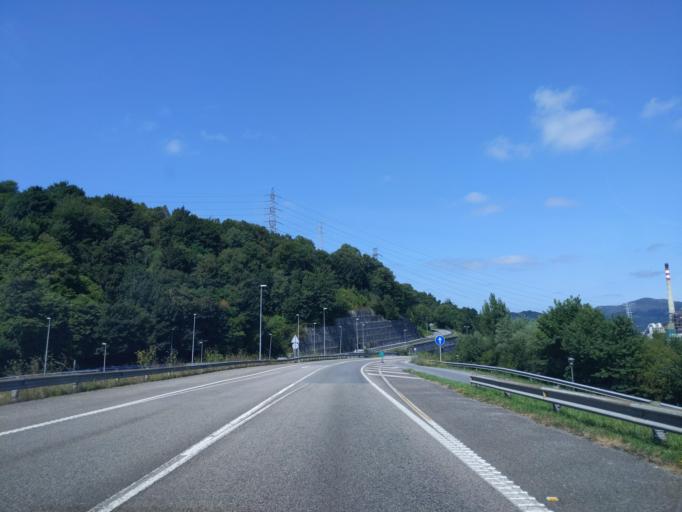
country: ES
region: Asturias
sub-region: Province of Asturias
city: Sama
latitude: 43.2997
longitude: -5.6894
